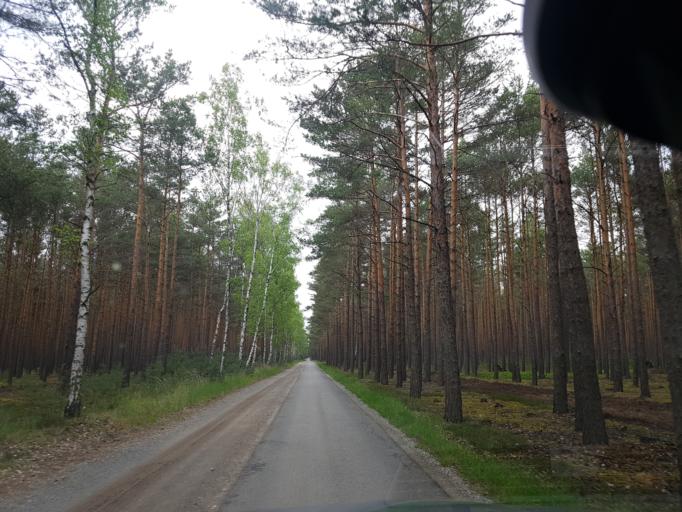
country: DE
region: Brandenburg
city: Crinitz
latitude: 51.6875
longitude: 13.7778
